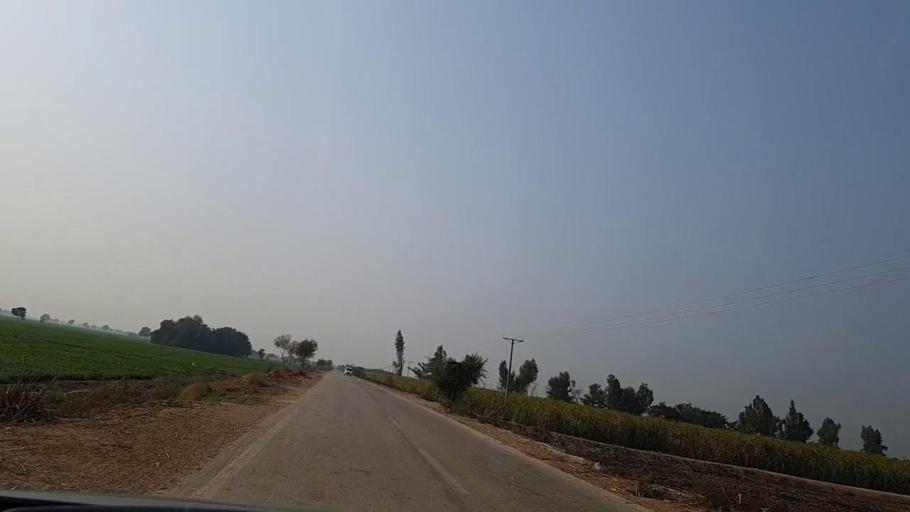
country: PK
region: Sindh
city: Sakrand
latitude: 26.1381
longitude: 68.1720
